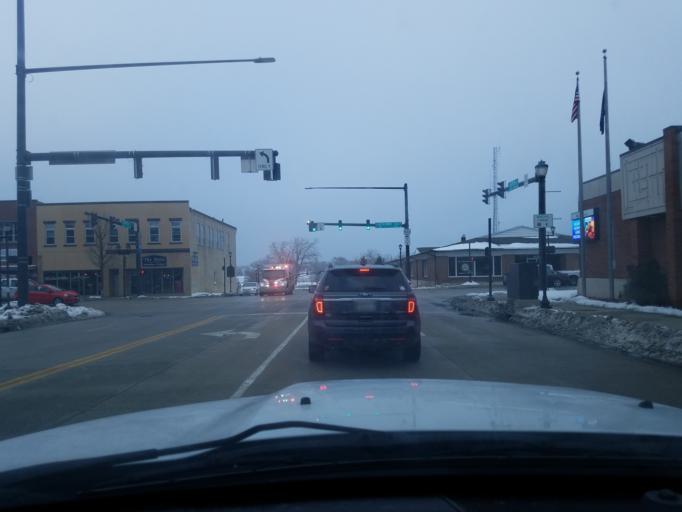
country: US
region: Indiana
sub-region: Saint Joseph County
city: Mishawaka
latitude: 41.6608
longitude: -86.1792
